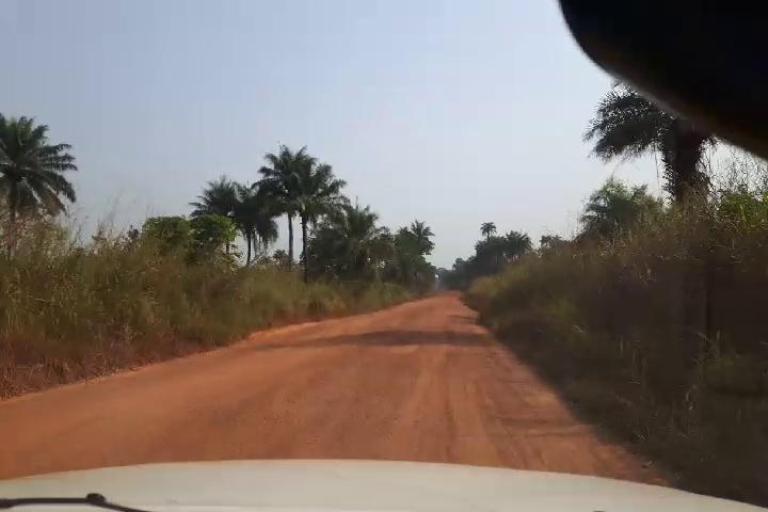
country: SL
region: Northern Province
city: Masingbi
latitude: 8.8157
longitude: -11.8601
